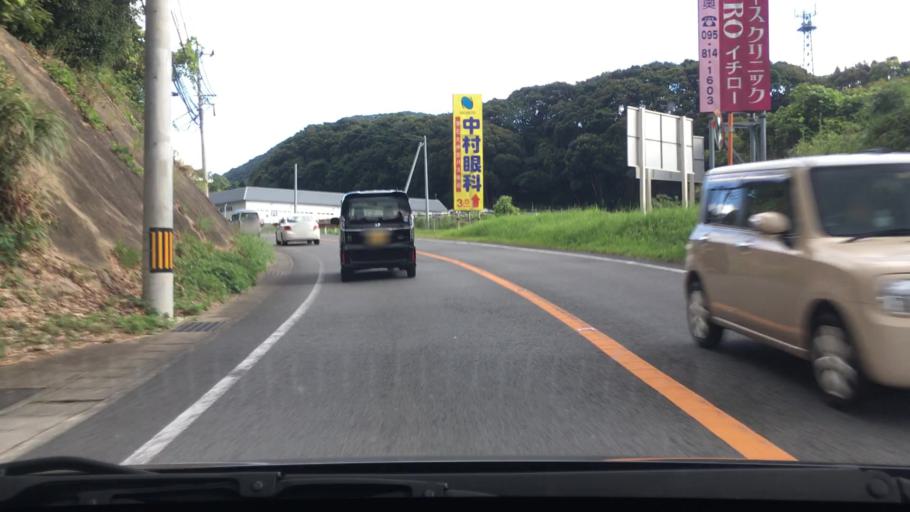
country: JP
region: Nagasaki
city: Togitsu
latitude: 32.8157
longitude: 129.8081
